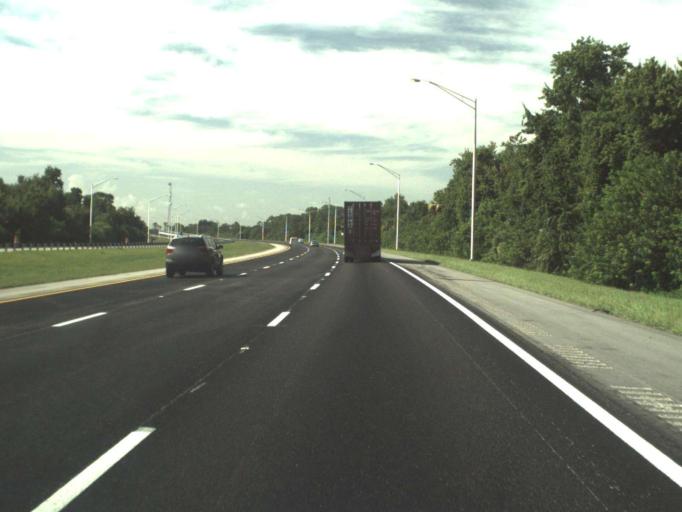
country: US
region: Florida
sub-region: Indian River County
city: West Vero Corridor
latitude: 27.6204
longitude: -80.5158
